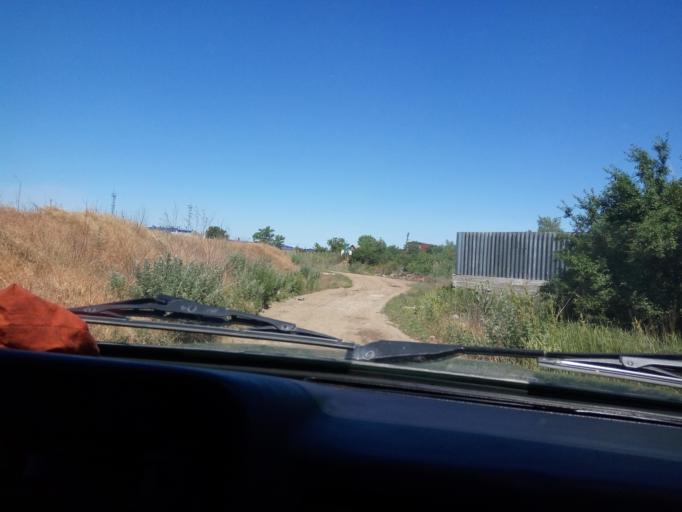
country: RU
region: Rostov
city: Bataysk
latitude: 47.0792
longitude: 39.7491
